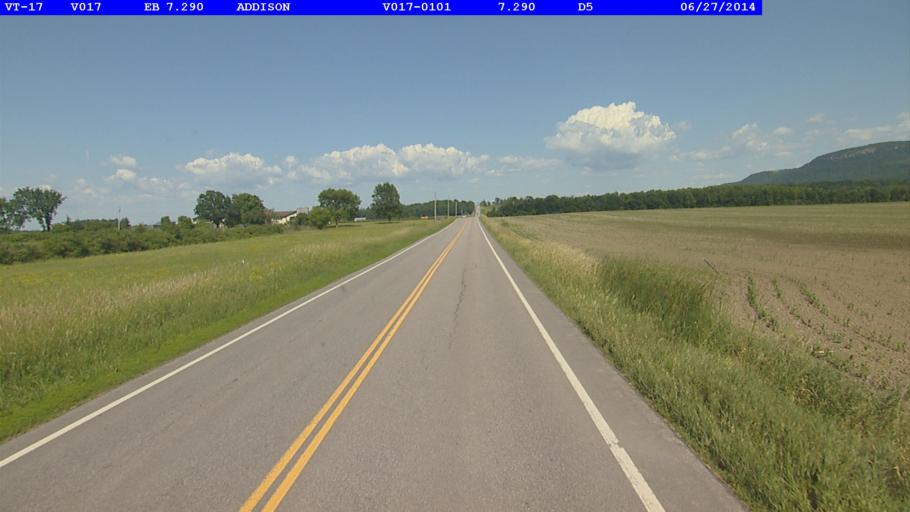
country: US
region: Vermont
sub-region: Addison County
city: Vergennes
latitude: 44.0871
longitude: -73.3243
